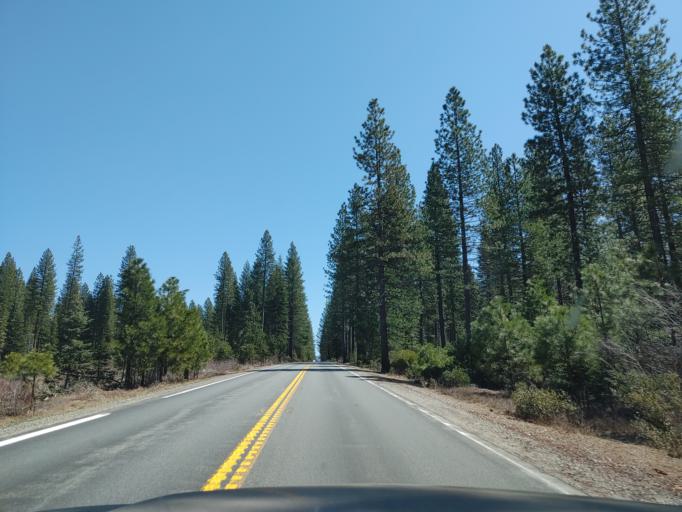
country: US
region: California
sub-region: Siskiyou County
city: McCloud
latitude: 41.2665
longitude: -121.8771
